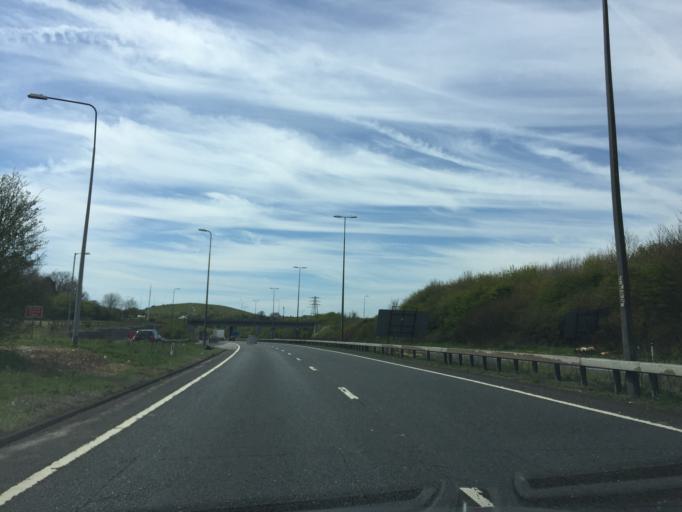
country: GB
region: England
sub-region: Kent
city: Hawkinge
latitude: 51.1068
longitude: 1.1741
